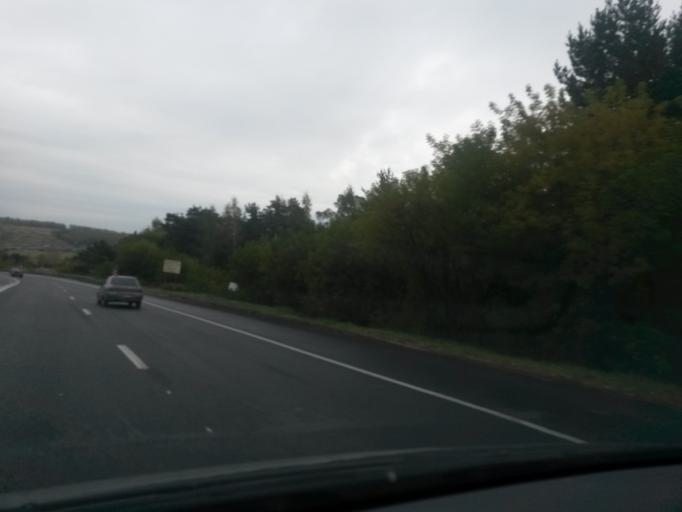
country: RU
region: Nizjnij Novgorod
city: Pamyat' Parizhskoy Kommuny
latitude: 56.0273
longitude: 44.6004
